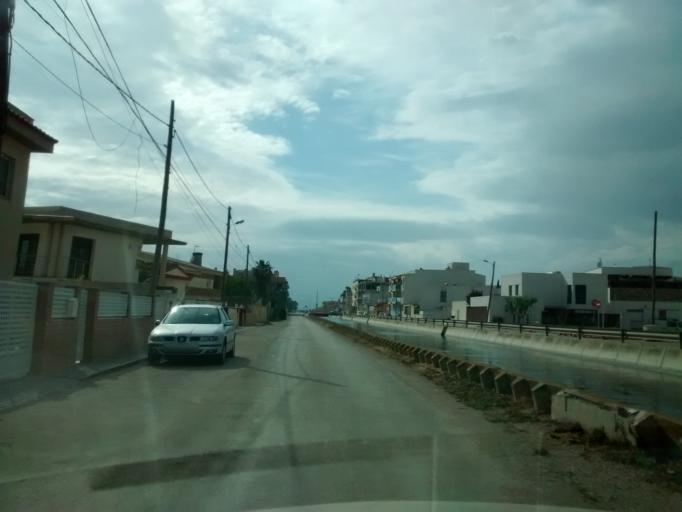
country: ES
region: Catalonia
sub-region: Provincia de Tarragona
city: Deltebre
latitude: 40.7033
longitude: 0.7205
